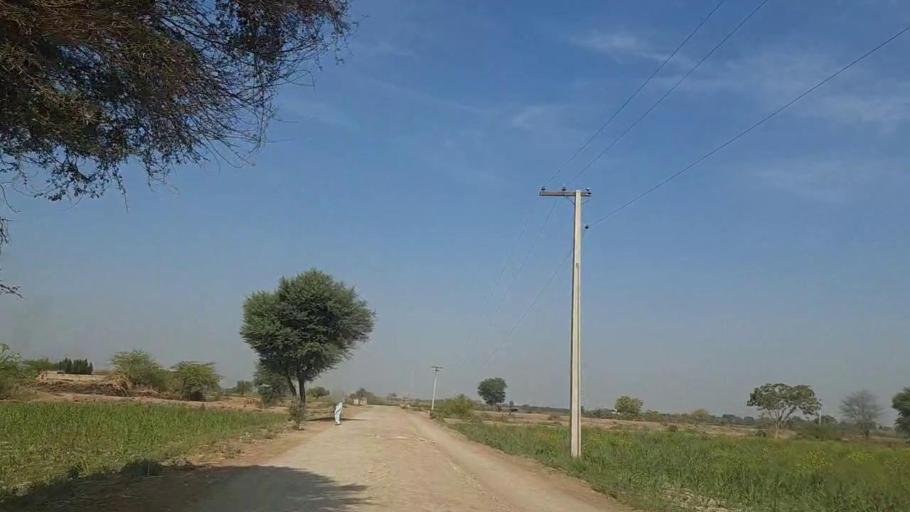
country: PK
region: Sindh
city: Mirpur Khas
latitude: 25.4906
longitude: 68.9631
